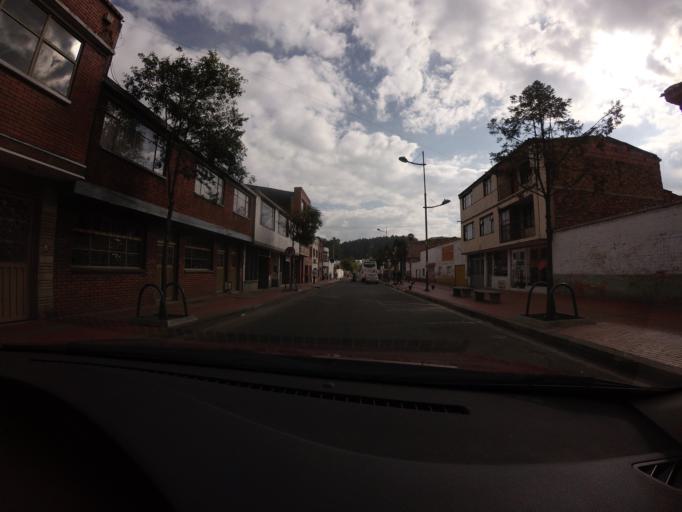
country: CO
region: Cundinamarca
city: Zipaquira
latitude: 5.0207
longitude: -74.0035
